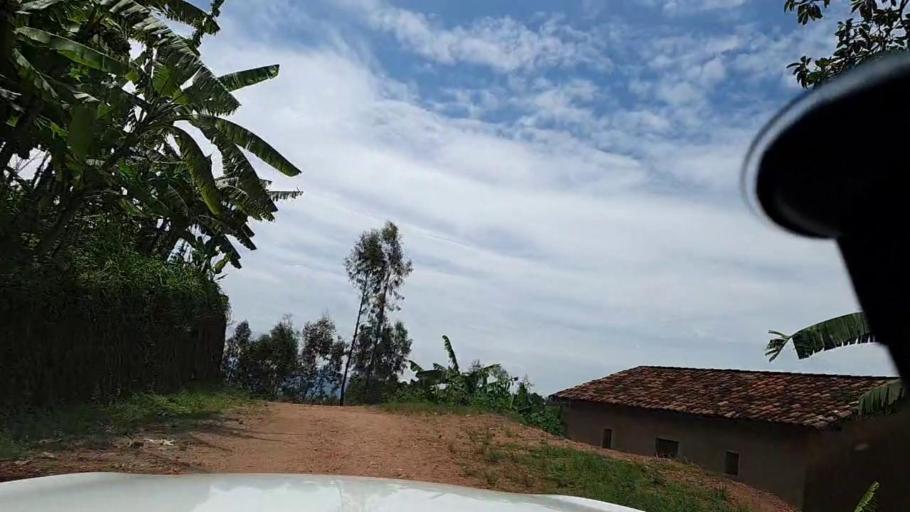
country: RW
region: Southern Province
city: Gitarama
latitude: -2.0805
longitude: 29.6651
